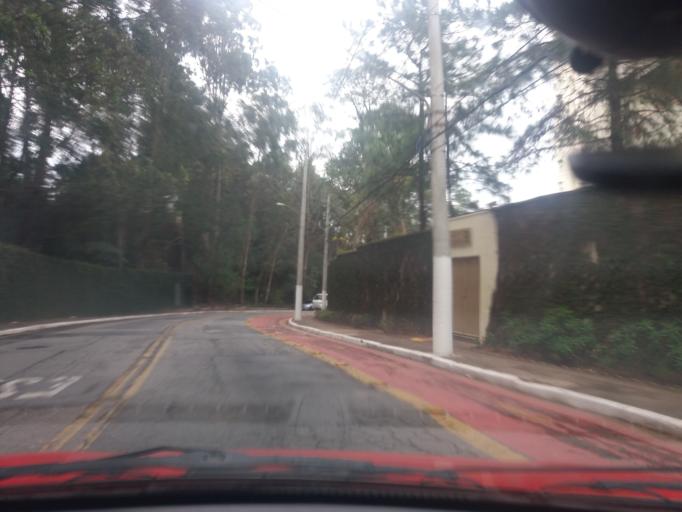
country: BR
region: Sao Paulo
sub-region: Taboao Da Serra
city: Taboao da Serra
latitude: -23.6151
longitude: -46.7464
